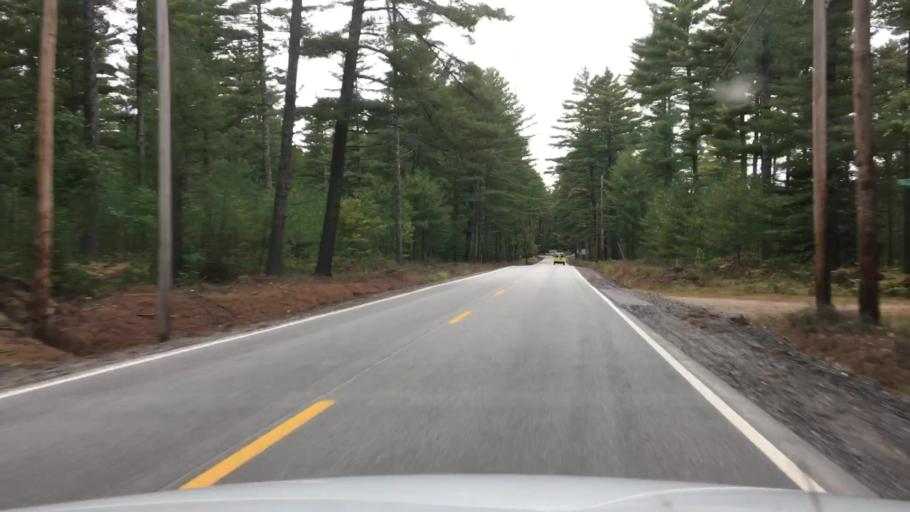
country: US
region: Maine
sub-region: Cumberland County
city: Harrison
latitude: 44.2271
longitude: -70.7015
